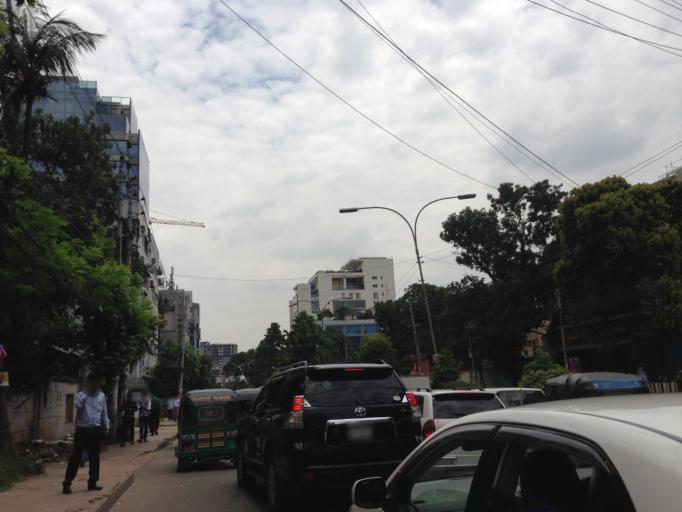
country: BD
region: Dhaka
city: Paltan
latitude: 23.7797
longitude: 90.4169
